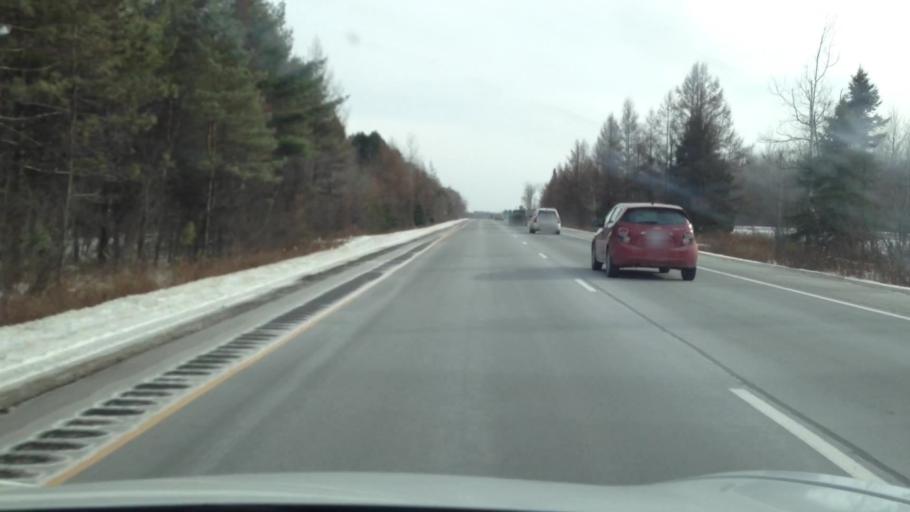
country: CA
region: Quebec
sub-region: Laurentides
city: Brownsburg-Chatham
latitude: 45.5570
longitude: -74.4651
